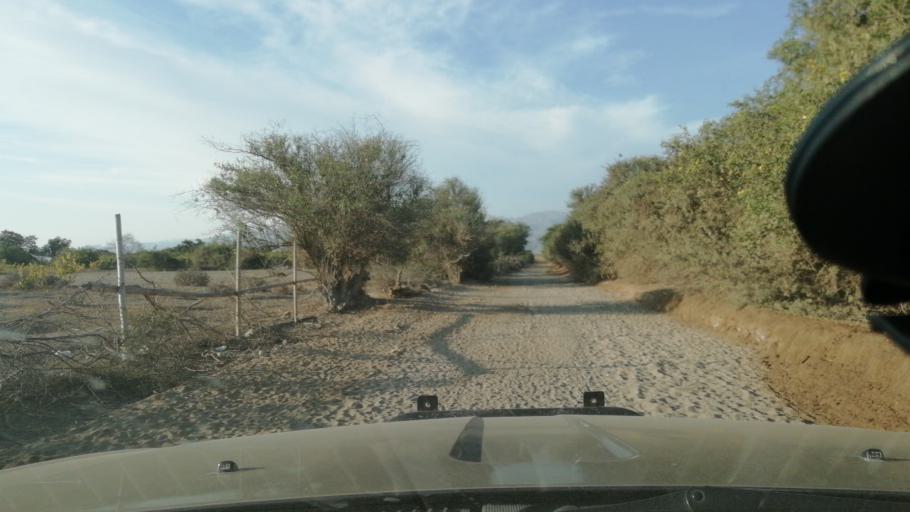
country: PE
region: Ica
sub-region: Provincia de Chincha
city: San Pedro
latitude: -13.3429
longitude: -76.1593
